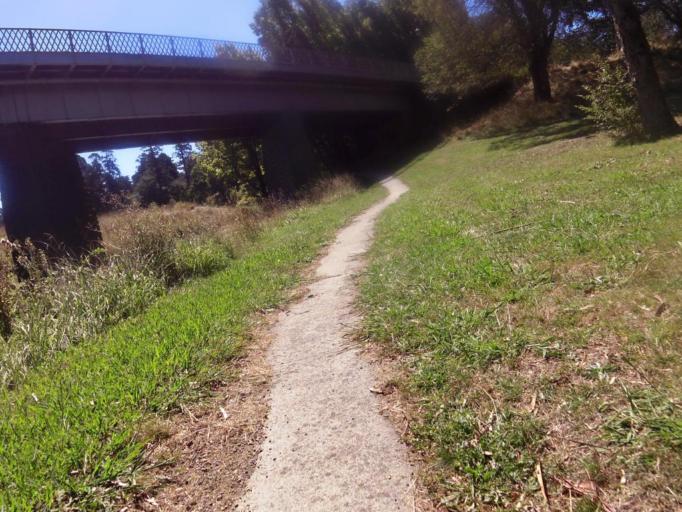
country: AU
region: Victoria
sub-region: Mount Alexander
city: Castlemaine
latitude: -37.2560
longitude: 144.4523
